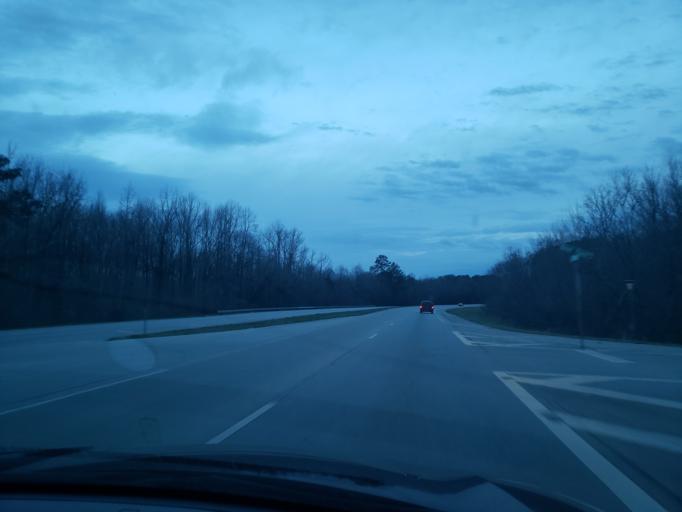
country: US
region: Alabama
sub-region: Lee County
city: Auburn
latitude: 32.6581
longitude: -85.4616
